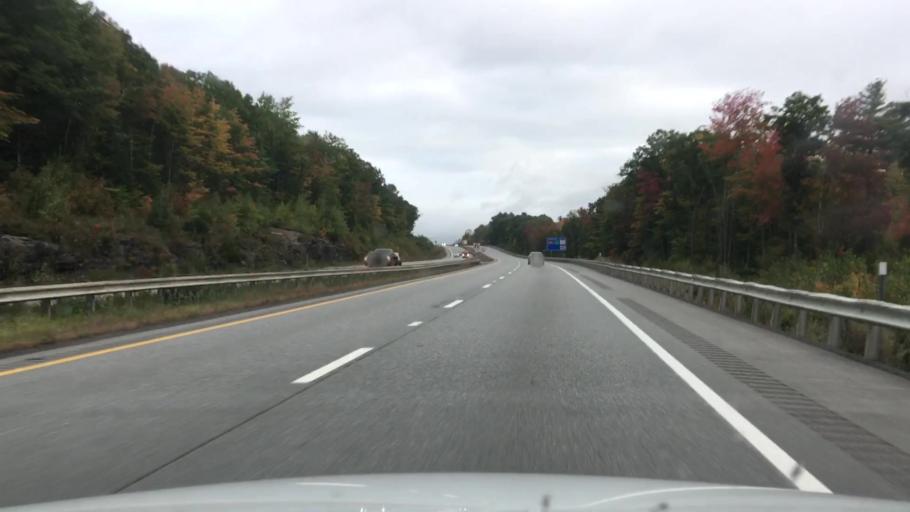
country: US
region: Maine
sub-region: Cumberland County
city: Cumberland Center
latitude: 43.8547
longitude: -70.3229
